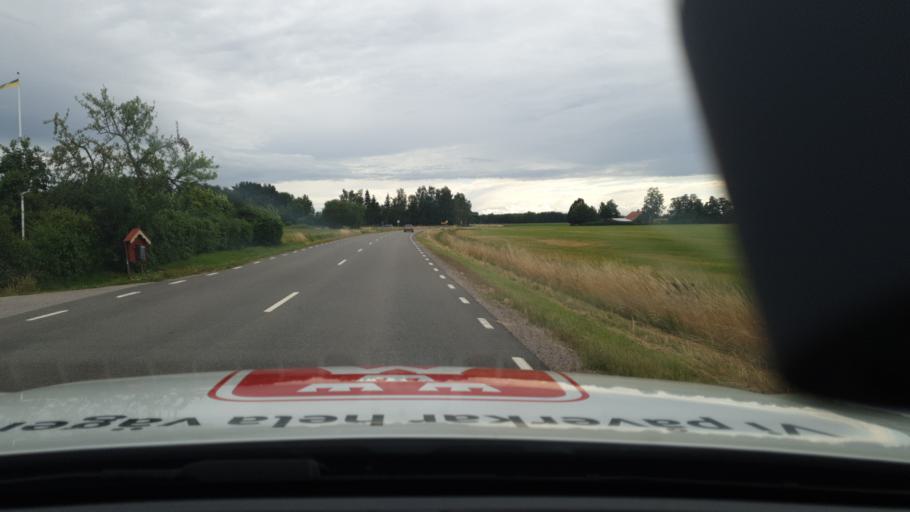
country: SE
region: Vaestra Goetaland
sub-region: Toreboda Kommun
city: Toereboda
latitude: 58.6666
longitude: 14.1311
